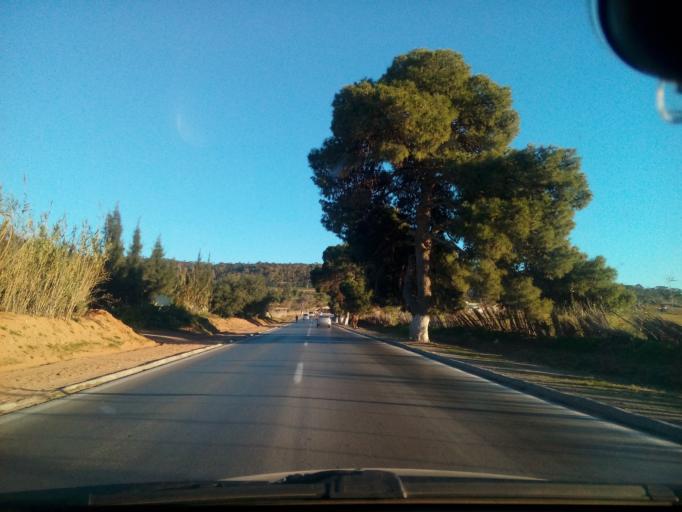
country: DZ
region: Mostaganem
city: Mostaganem
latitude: 35.7733
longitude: 0.1996
